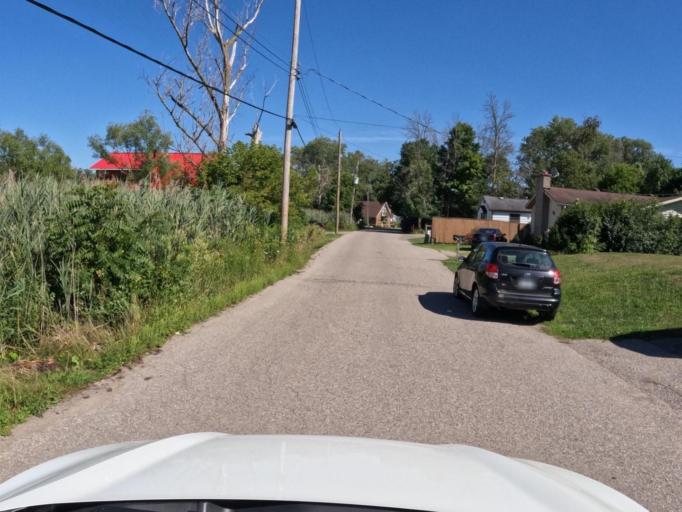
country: CA
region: Ontario
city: Cambridge
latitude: 43.4219
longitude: -80.2746
